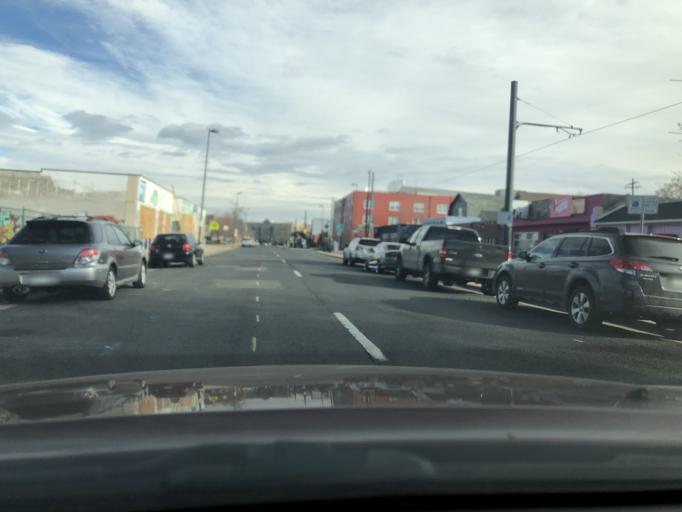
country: US
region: Colorado
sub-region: Denver County
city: Denver
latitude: 39.7561
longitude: -104.9765
